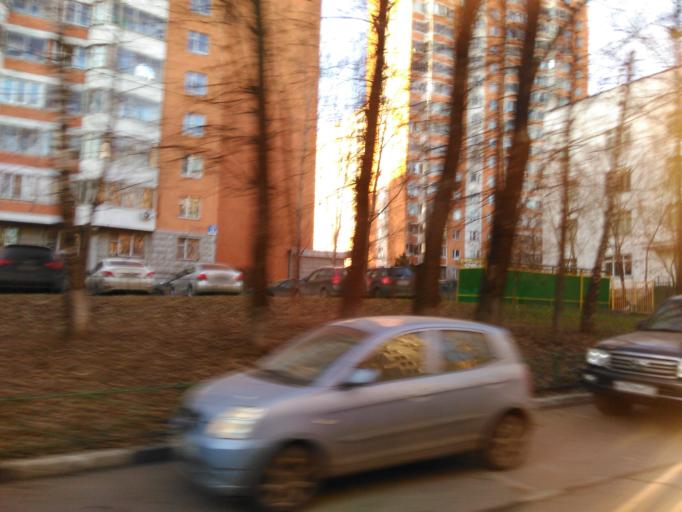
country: RU
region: Moscow
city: Nagornyy
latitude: 55.6477
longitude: 37.6098
